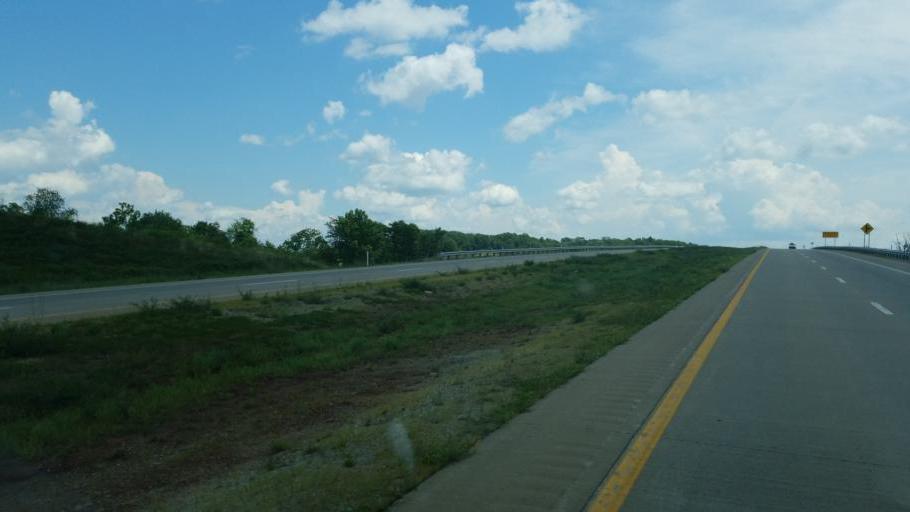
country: US
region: West Virginia
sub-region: Mason County
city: Point Pleasant
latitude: 38.7682
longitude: -82.0307
